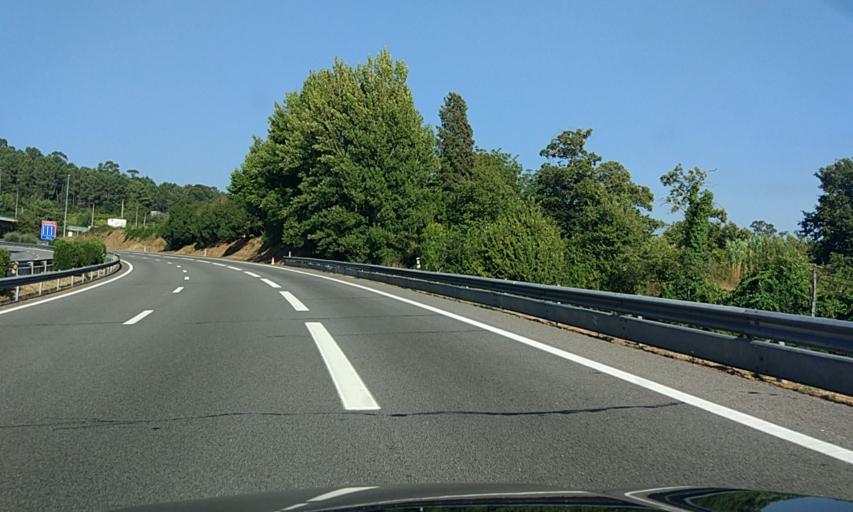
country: PT
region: Porto
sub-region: Marco de Canaveses
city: Marco de Canavezes
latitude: 41.2257
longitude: -8.1542
